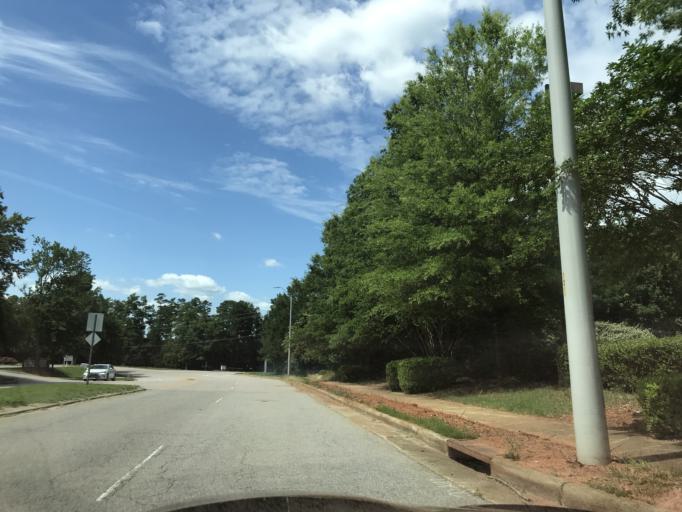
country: US
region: North Carolina
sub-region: Wake County
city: West Raleigh
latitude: 35.9055
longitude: -78.6580
